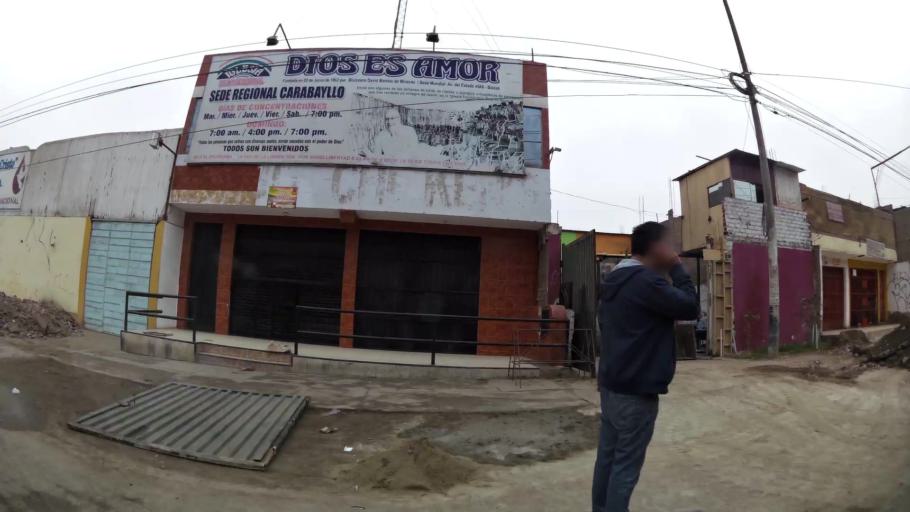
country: PE
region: Lima
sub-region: Lima
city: Urb. Santo Domingo
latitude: -11.8961
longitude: -77.0297
